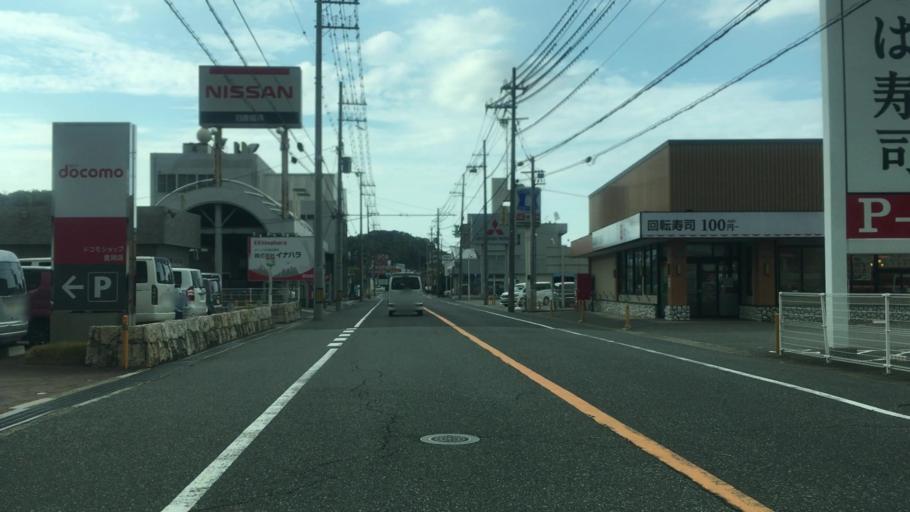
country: JP
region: Hyogo
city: Toyooka
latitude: 35.5292
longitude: 134.8202
